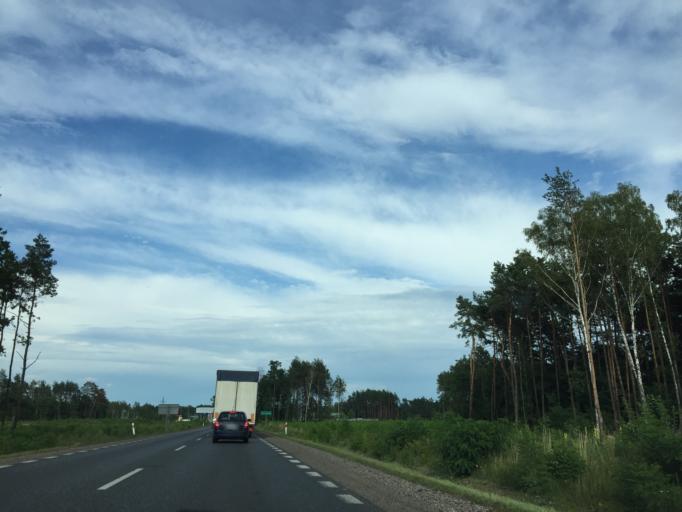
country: PL
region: Masovian Voivodeship
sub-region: Powiat piaseczynski
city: Gora Kalwaria
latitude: 51.9701
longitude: 21.1927
